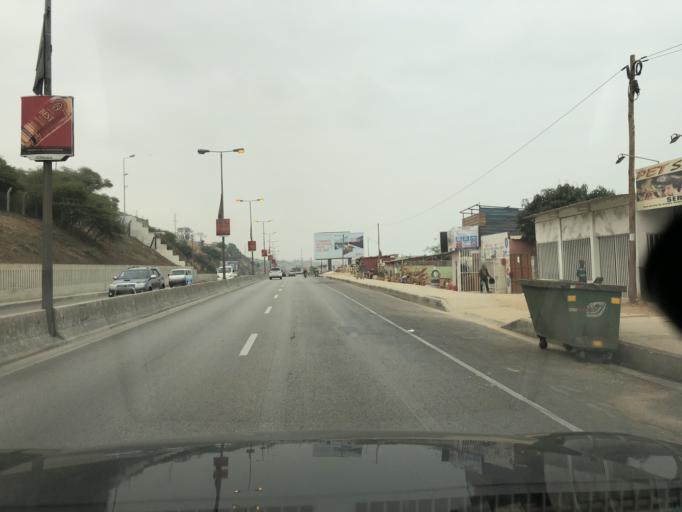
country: AO
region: Luanda
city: Luanda
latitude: -8.8631
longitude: 13.2024
